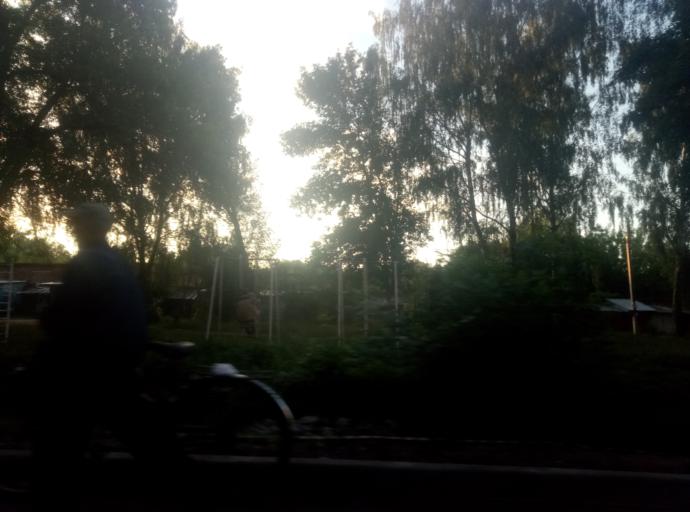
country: RU
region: Tula
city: Kireyevsk
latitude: 53.9274
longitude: 37.9367
